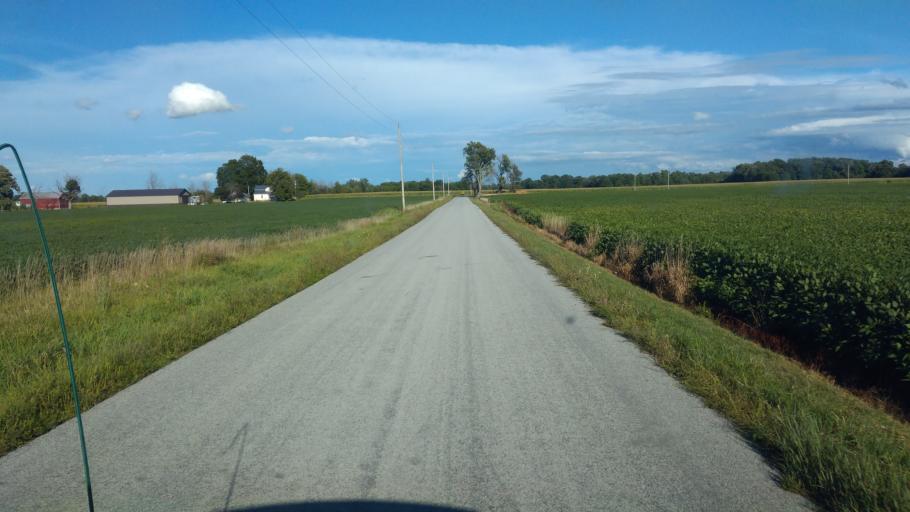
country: US
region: Ohio
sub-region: Hardin County
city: Forest
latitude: 40.7605
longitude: -83.6089
